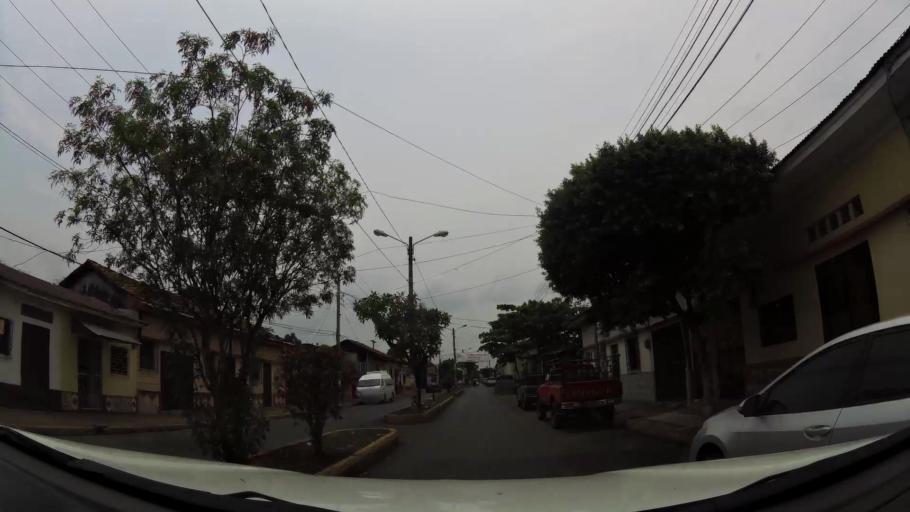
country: NI
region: Leon
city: Leon
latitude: 12.4346
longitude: -86.8939
